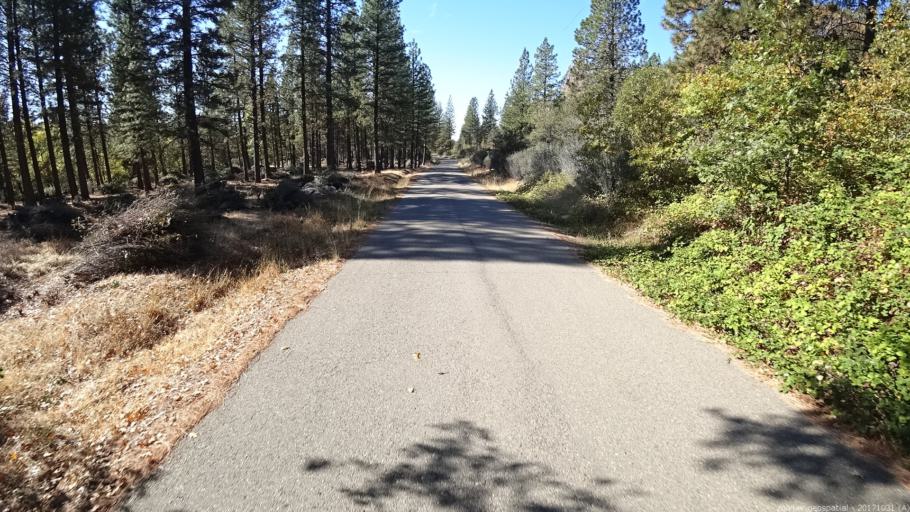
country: US
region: California
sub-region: Shasta County
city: Shingletown
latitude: 40.4467
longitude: -121.8140
